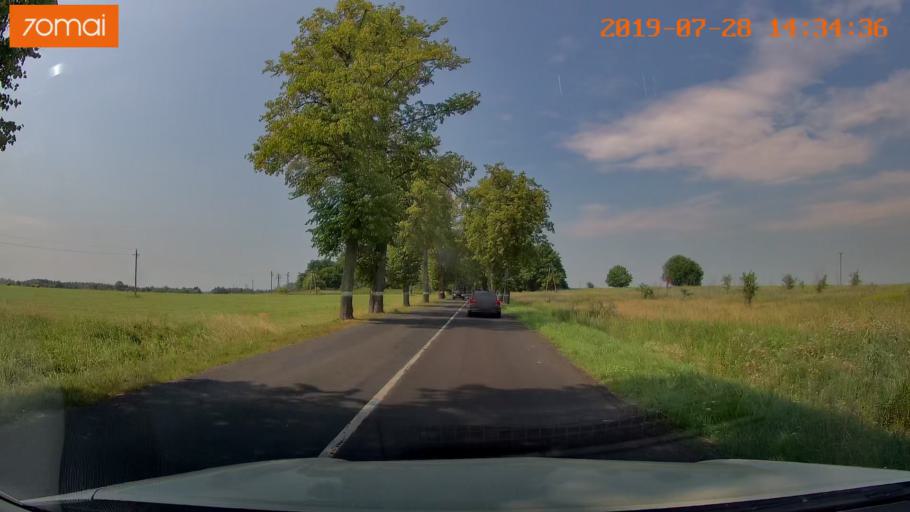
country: RU
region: Kaliningrad
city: Primorsk
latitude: 54.8262
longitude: 20.0165
